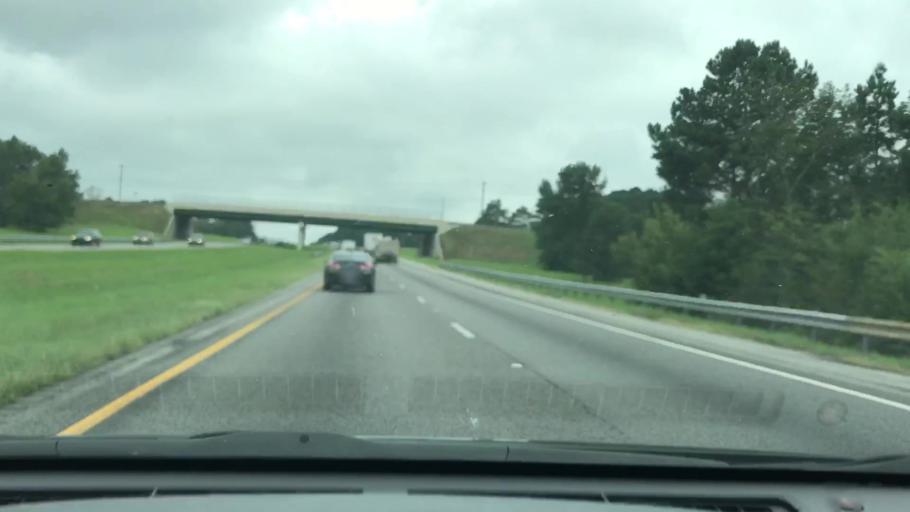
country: US
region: Georgia
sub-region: Walton County
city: Social Circle
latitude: 33.6125
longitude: -83.7478
